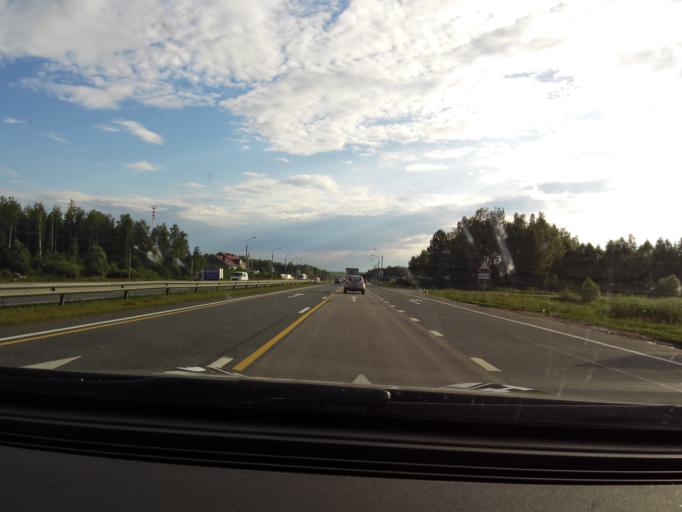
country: RU
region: Vladimir
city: Sudogda
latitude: 56.1348
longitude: 40.8862
